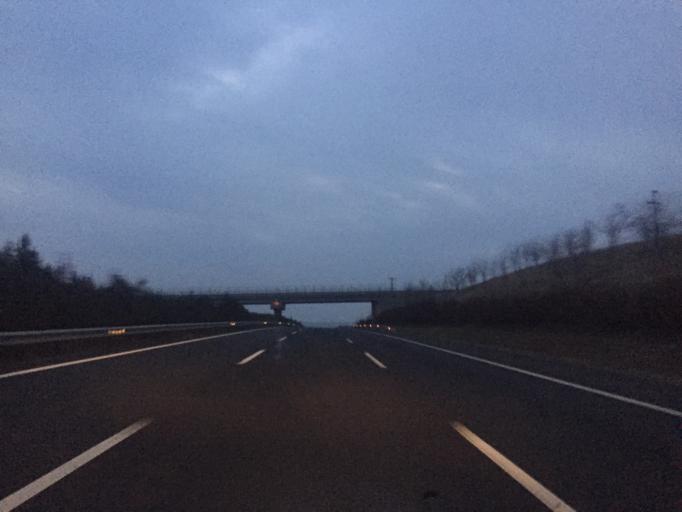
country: TR
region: Sanliurfa
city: Camlidere
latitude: 37.1986
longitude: 38.9328
